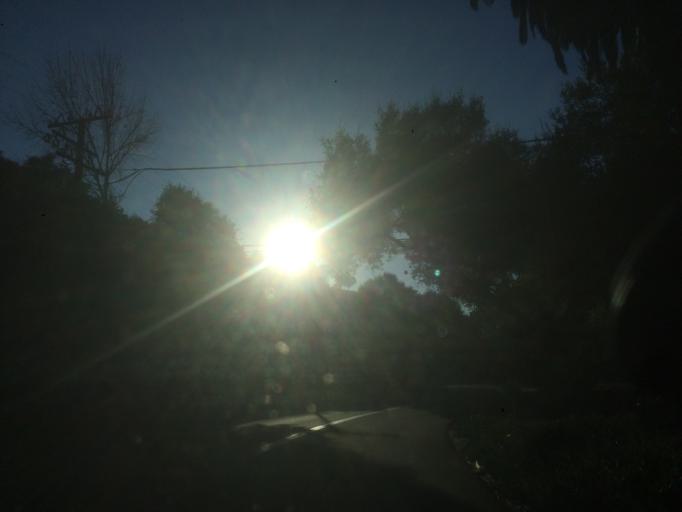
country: US
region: California
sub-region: Santa Barbara County
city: Mission Canyon
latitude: 34.4221
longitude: -119.7655
